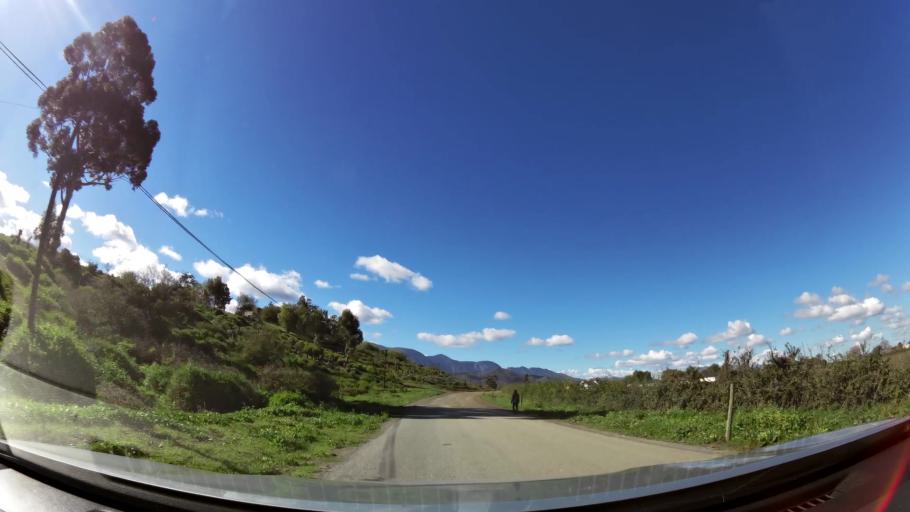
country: ZA
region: Western Cape
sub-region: Cape Winelands District Municipality
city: Ashton
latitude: -33.7944
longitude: 19.8976
